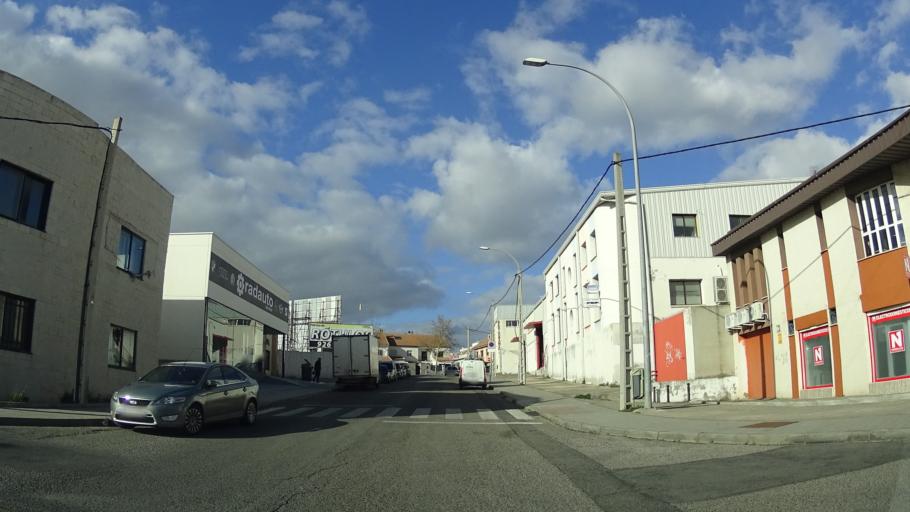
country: ES
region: Castille-La Mancha
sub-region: Provincia de Ciudad Real
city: Ciudad Real
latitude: 38.9769
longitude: -3.9308
